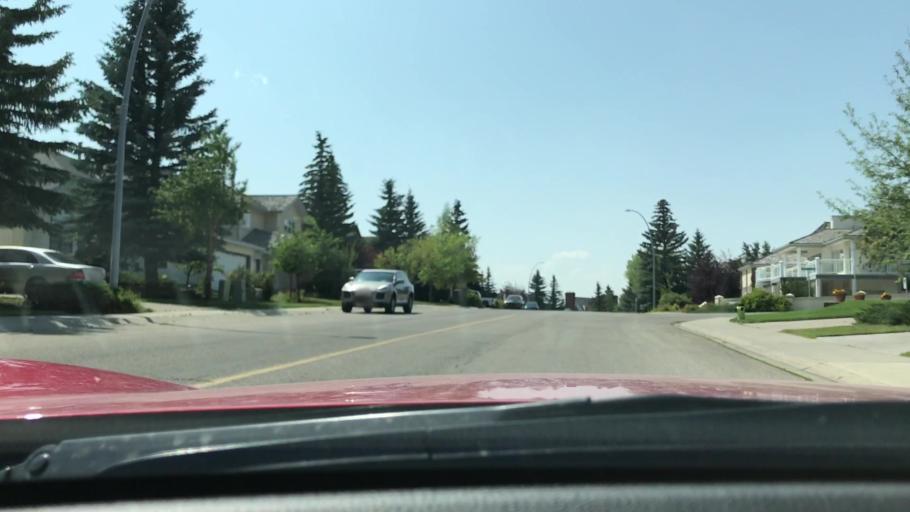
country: CA
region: Alberta
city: Calgary
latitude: 51.0219
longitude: -114.1723
